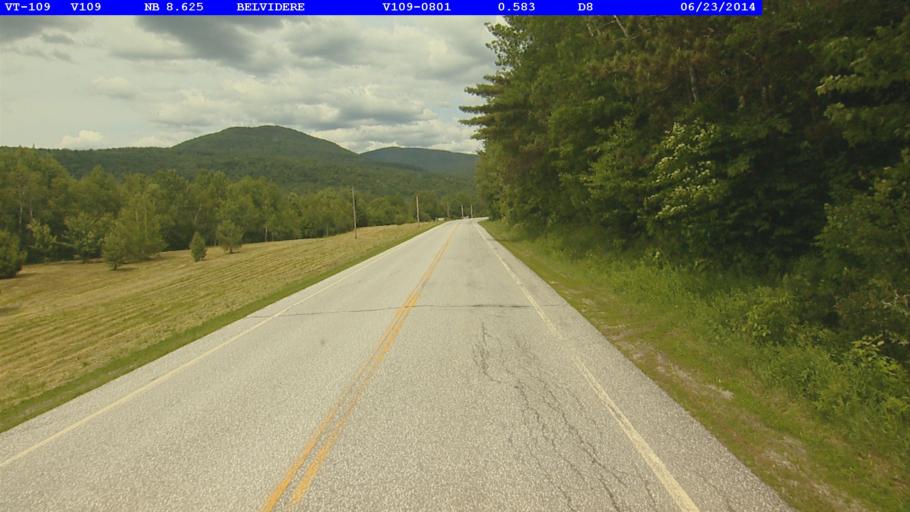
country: US
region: Vermont
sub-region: Lamoille County
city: Johnson
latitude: 44.7390
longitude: -72.7331
